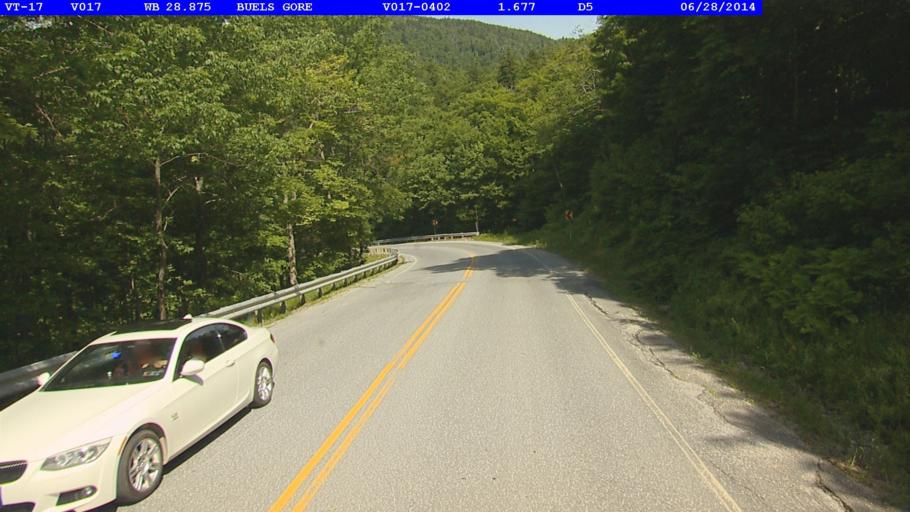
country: US
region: Vermont
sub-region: Addison County
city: Bristol
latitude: 44.2156
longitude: -72.9420
